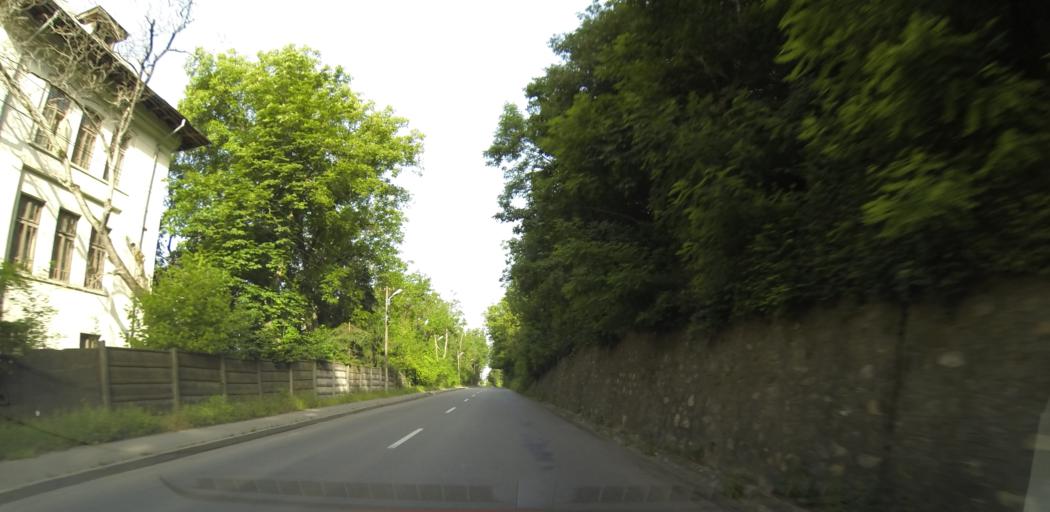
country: RO
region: Valcea
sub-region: Comuna Bujoreni
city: Bujoreni
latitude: 45.1088
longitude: 24.3361
